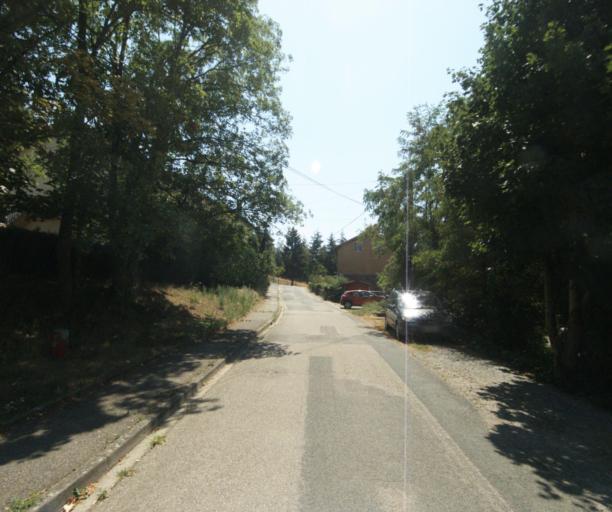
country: FR
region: Rhone-Alpes
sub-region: Departement du Rhone
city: Saint-Pierre-la-Palud
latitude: 45.7987
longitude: 4.6097
